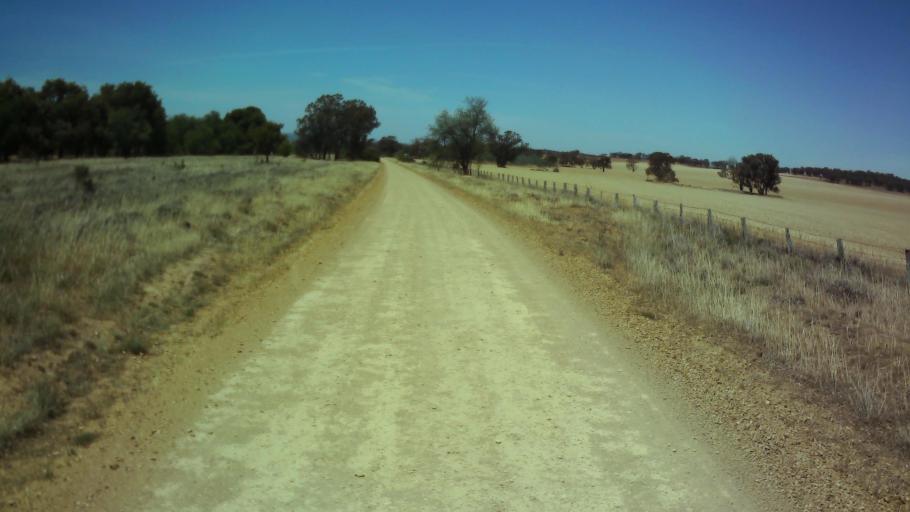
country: AU
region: New South Wales
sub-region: Weddin
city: Grenfell
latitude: -33.9241
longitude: 148.1802
